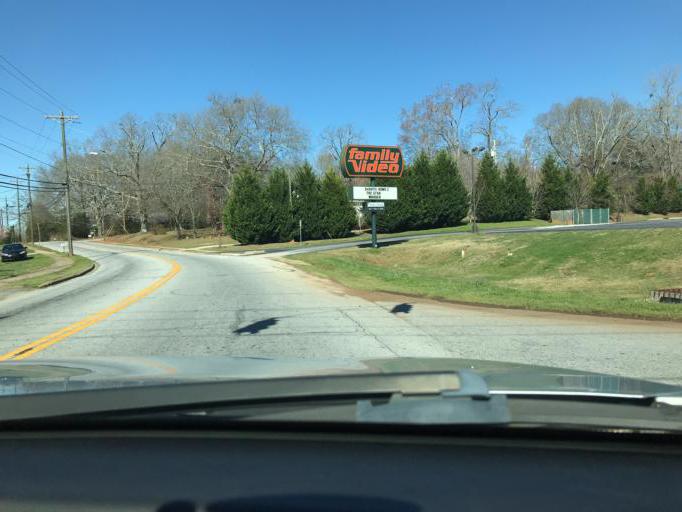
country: US
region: South Carolina
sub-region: Laurens County
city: Laurens
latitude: 34.4987
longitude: -81.9972
